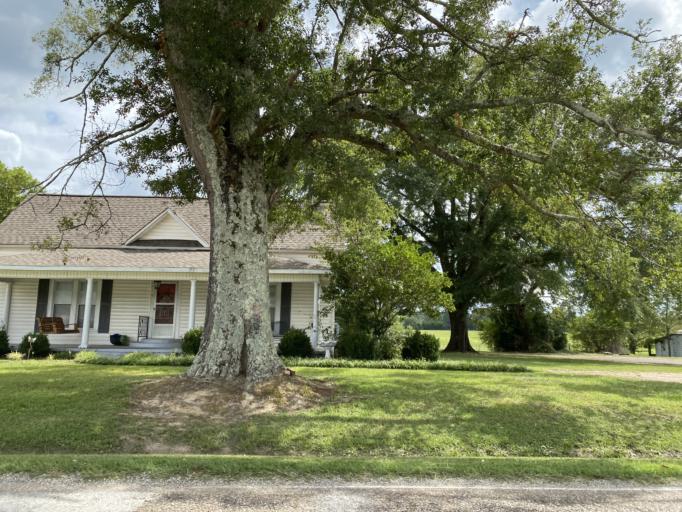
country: US
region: Mississippi
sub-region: Monroe County
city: Amory
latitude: 33.9769
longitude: -88.4187
